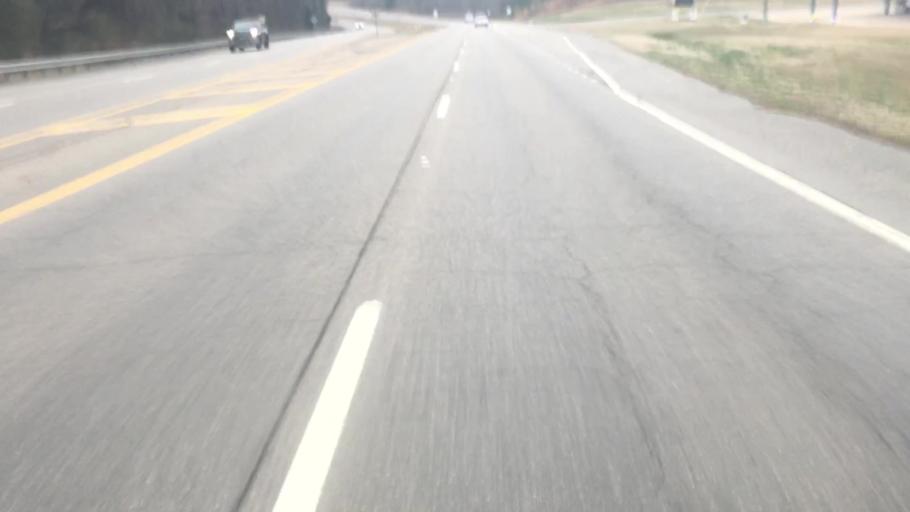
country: US
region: Alabama
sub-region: Walker County
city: Sumiton
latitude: 33.7511
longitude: -87.0589
